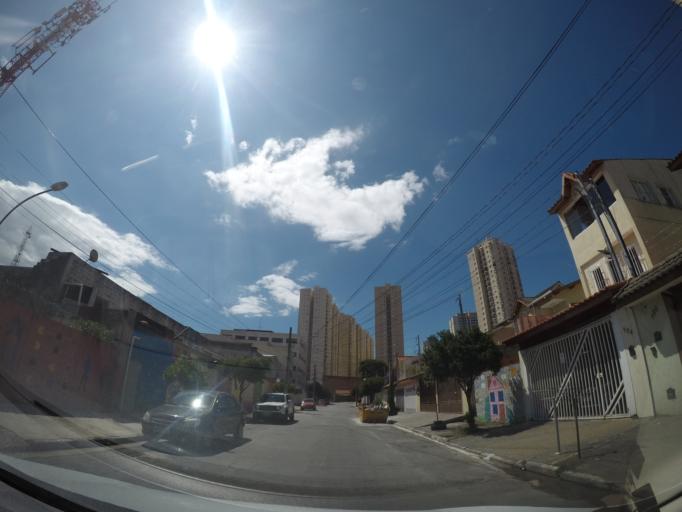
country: BR
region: Sao Paulo
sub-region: Guarulhos
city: Guarulhos
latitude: -23.4632
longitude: -46.5368
